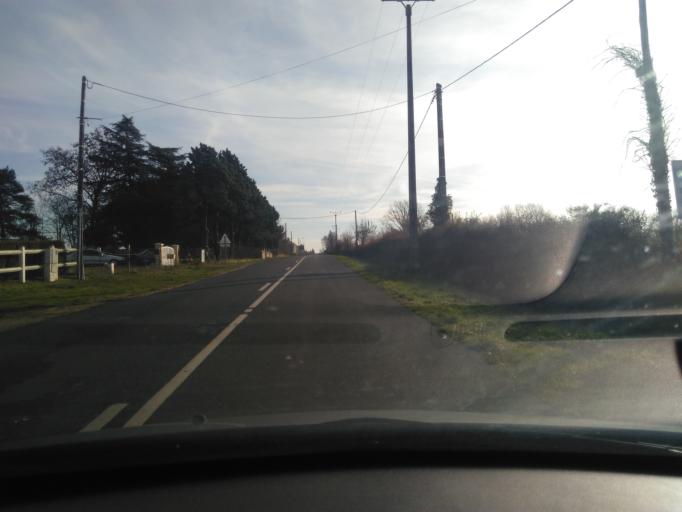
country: FR
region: Centre
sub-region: Departement du Cher
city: Chateaumeillant
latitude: 46.6316
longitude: 2.1347
